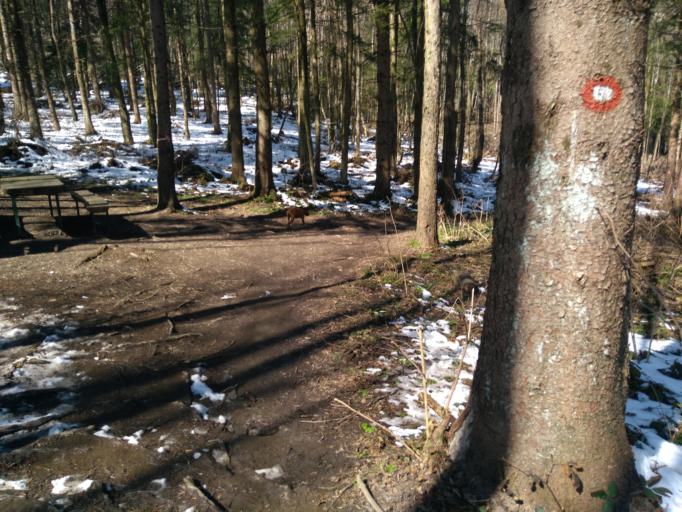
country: HR
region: Varazdinska
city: Ivanec
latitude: 46.1840
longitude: 16.1097
